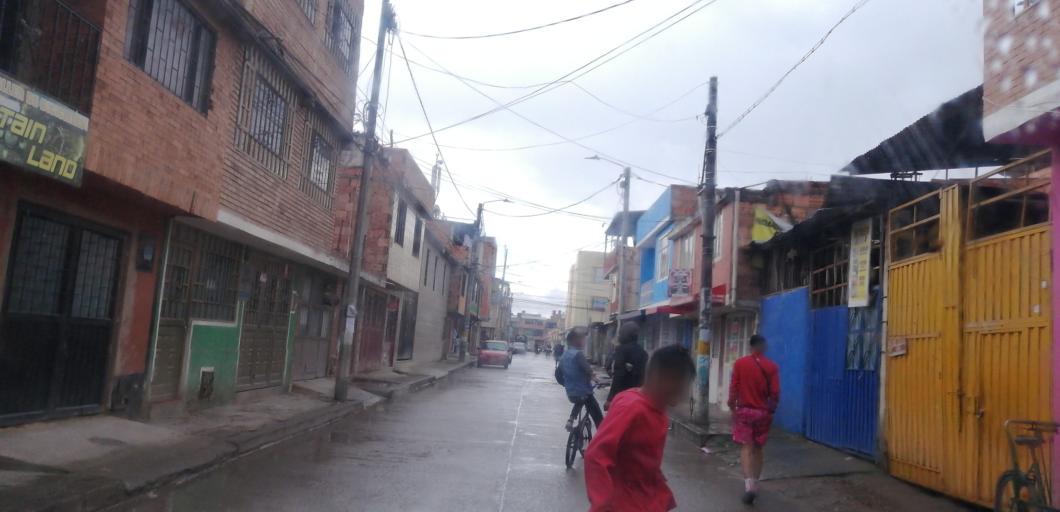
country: CO
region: Cundinamarca
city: Madrid
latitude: 4.7258
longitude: -74.2840
